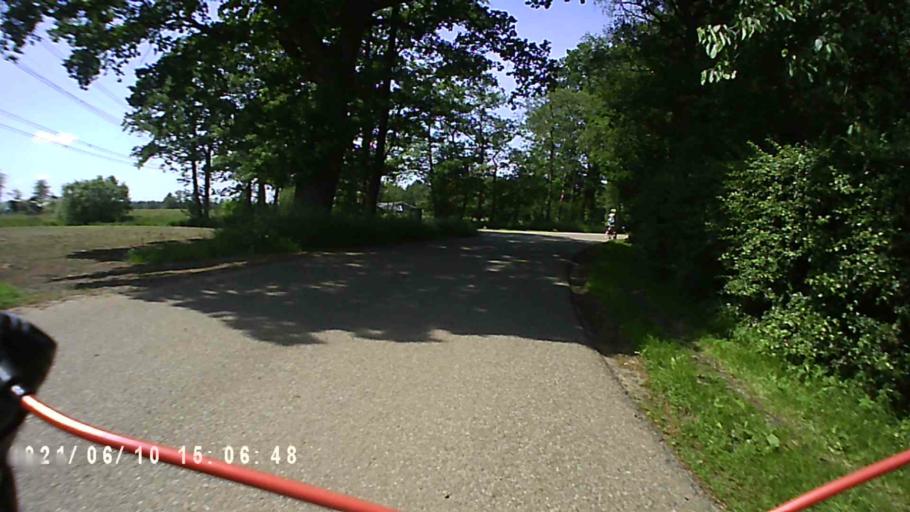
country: NL
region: Friesland
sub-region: Gemeente Achtkarspelen
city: Surhuizum
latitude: 53.1936
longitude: 6.2115
